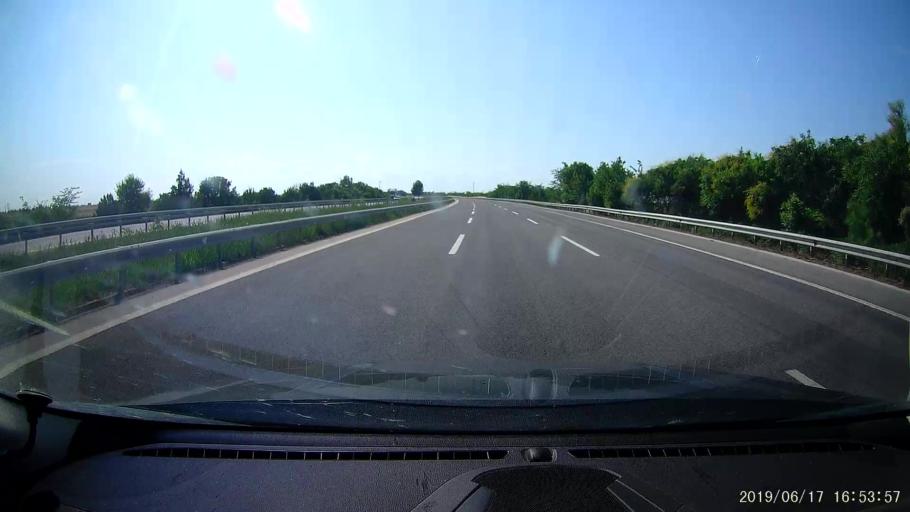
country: TR
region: Kirklareli
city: Inece
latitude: 41.5700
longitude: 27.0100
